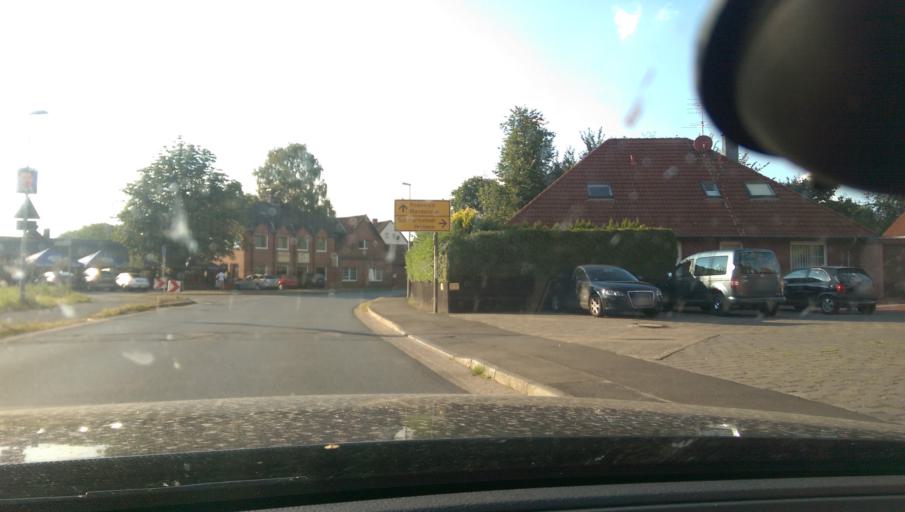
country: DE
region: Lower Saxony
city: Schwarmstedt
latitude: 52.5837
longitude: 9.5855
